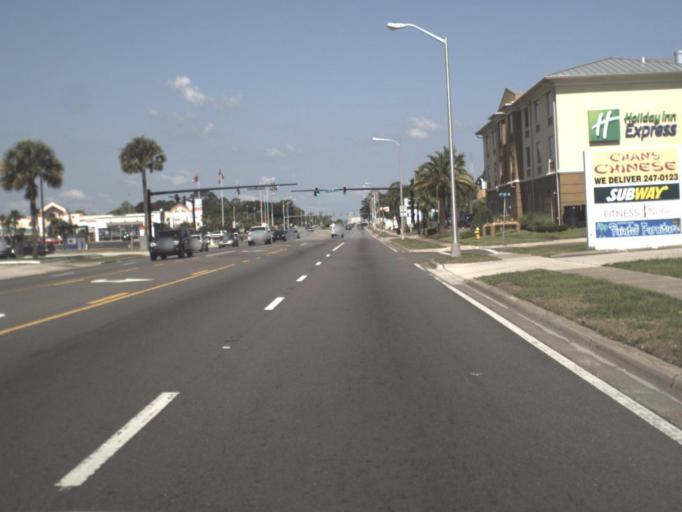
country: US
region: Florida
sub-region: Duval County
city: Jacksonville Beach
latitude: 30.2883
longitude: -81.4003
